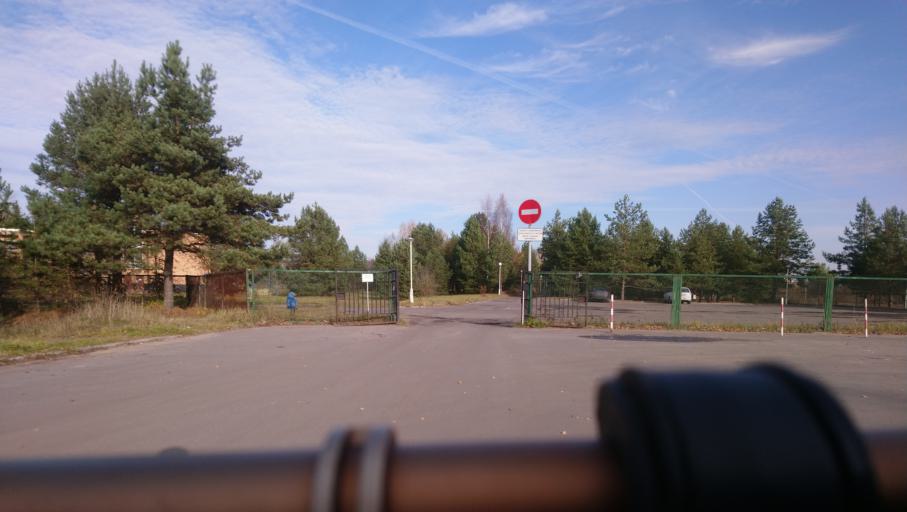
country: RU
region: Moskovskaya
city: Dubna
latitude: 56.7771
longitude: 37.2364
